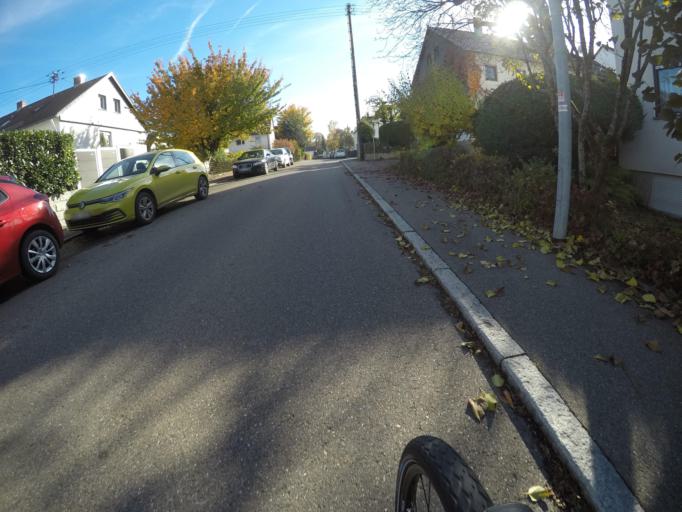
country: DE
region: Baden-Wuerttemberg
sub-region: Regierungsbezirk Stuttgart
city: Leinfelden-Echterdingen
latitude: 48.6909
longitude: 9.1438
